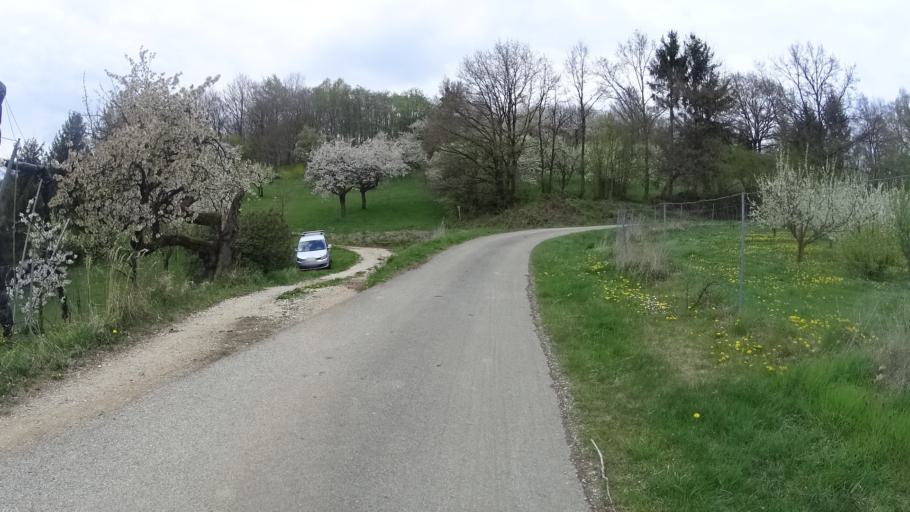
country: DE
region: Bavaria
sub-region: Upper Franconia
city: Kleinsendelbach
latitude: 49.6216
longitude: 11.1820
